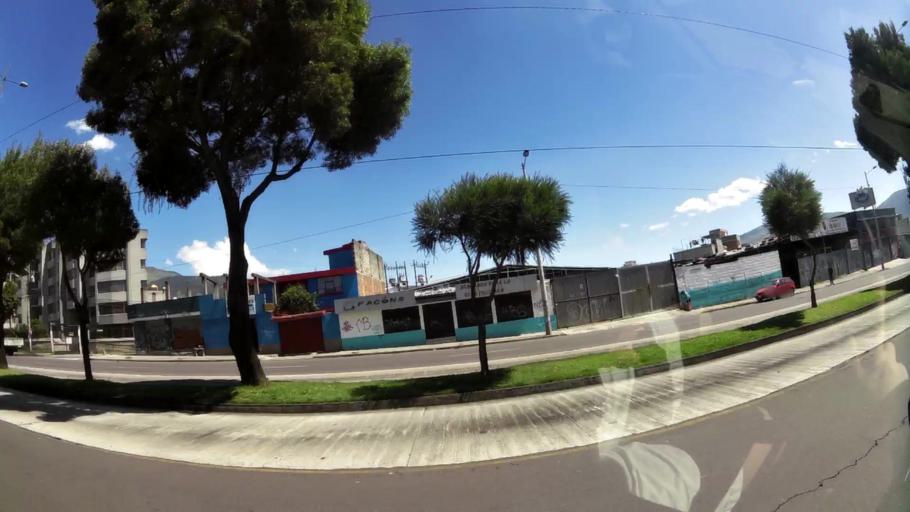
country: EC
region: Pichincha
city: Quito
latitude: -0.1180
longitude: -78.4914
